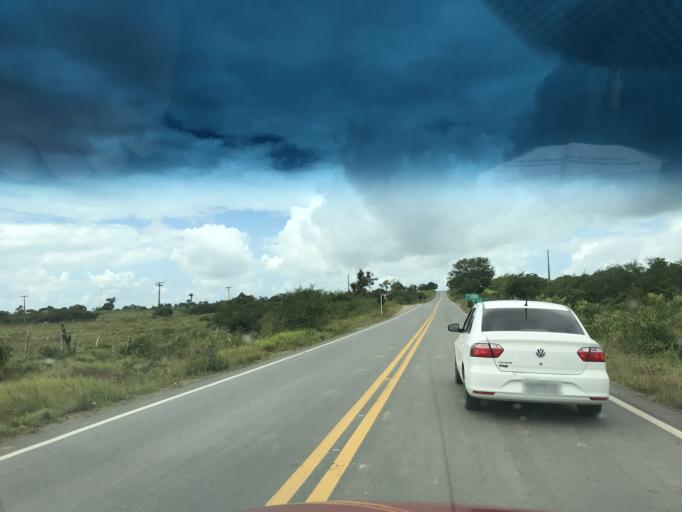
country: BR
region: Bahia
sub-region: Conceicao Do Almeida
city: Conceicao do Almeida
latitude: -12.6812
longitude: -39.2557
